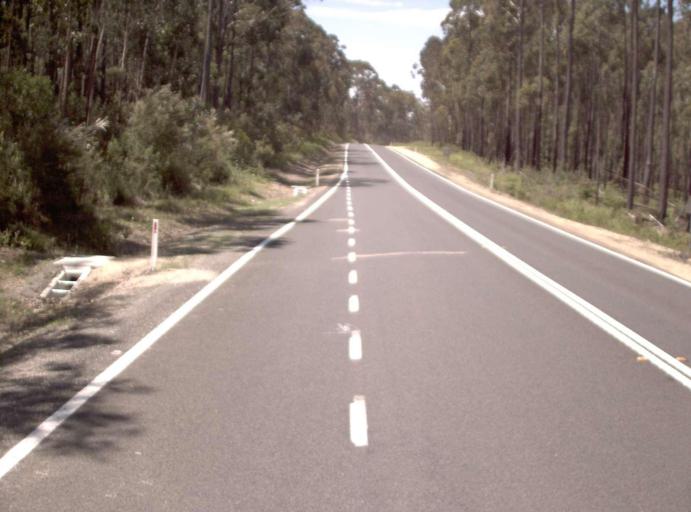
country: AU
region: New South Wales
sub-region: Bombala
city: Bombala
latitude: -37.6478
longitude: 148.8310
